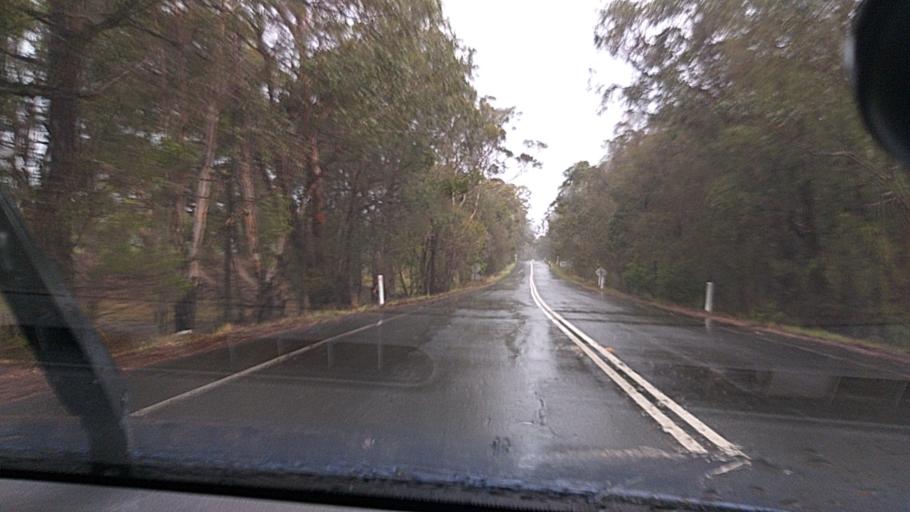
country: AU
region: New South Wales
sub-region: Wollondilly
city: Douglas Park
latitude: -34.2398
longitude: 150.7284
